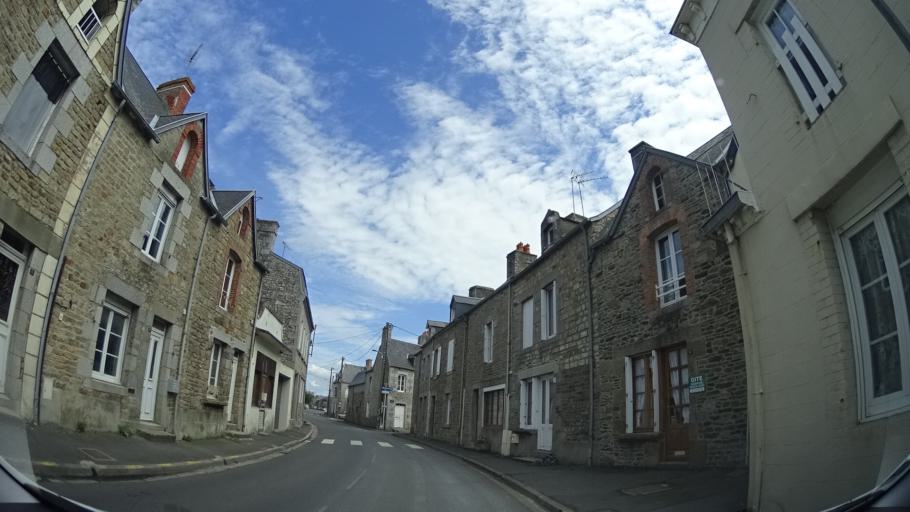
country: FR
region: Lower Normandy
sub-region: Departement de la Manche
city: Sartilly
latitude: 48.6843
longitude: -1.4776
